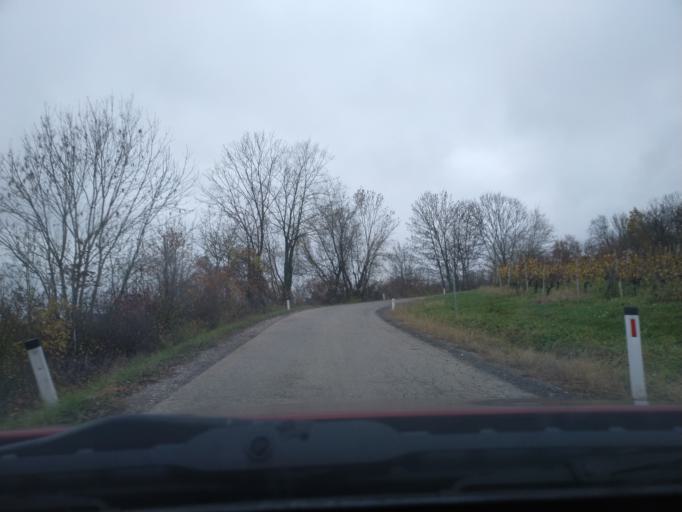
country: SI
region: Kungota
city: Zgornja Kungota
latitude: 46.6766
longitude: 15.6096
